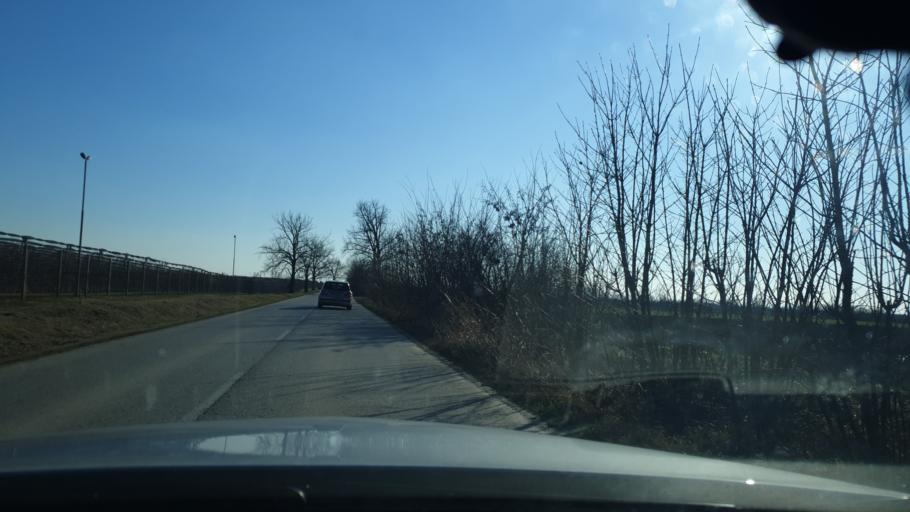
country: RS
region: Autonomna Pokrajina Vojvodina
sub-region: Sremski Okrug
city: Ruma
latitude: 45.0489
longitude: 19.8060
